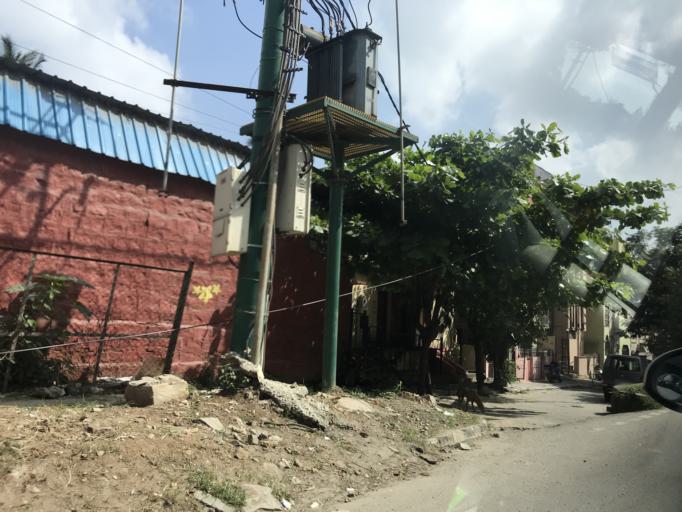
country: IN
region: Karnataka
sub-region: Bangalore Urban
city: Bangalore
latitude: 12.9786
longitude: 77.5647
